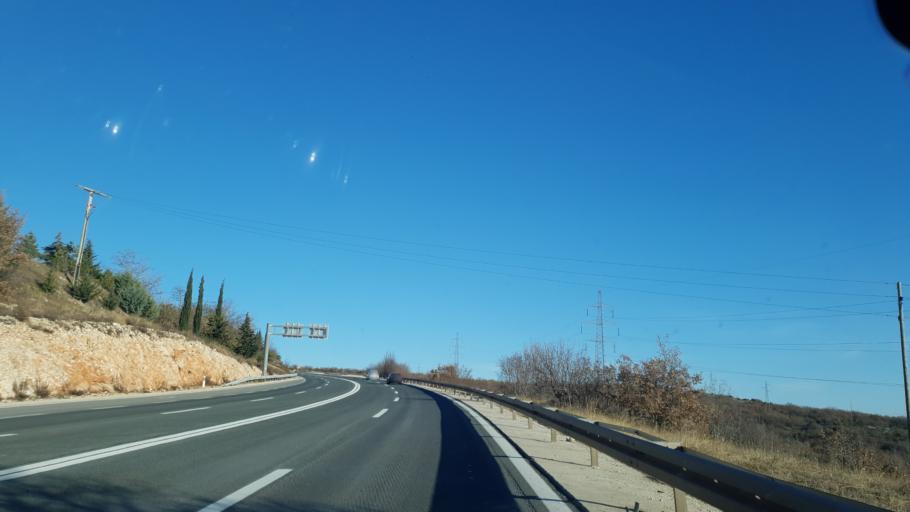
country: HR
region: Splitsko-Dalmatinska
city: Dugopolje
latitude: 43.6067
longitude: 16.5957
